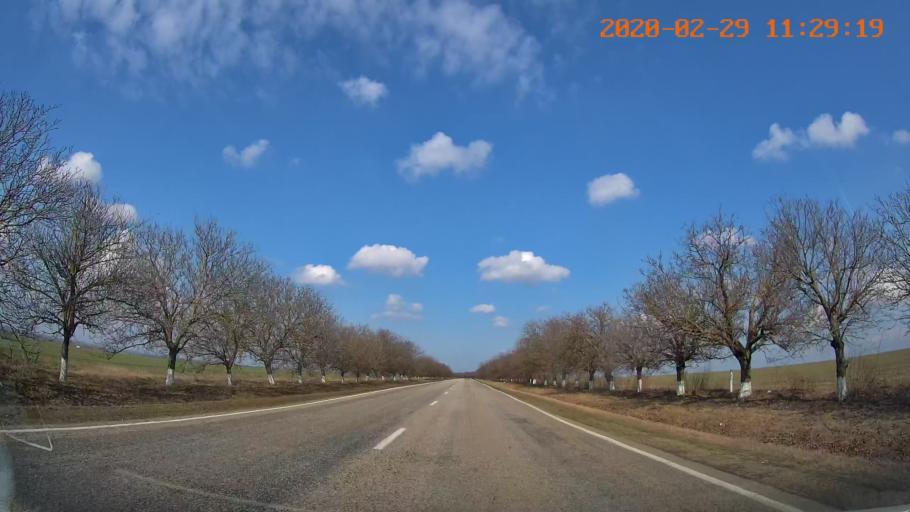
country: MD
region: Telenesti
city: Cocieri
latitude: 47.4928
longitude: 29.1265
